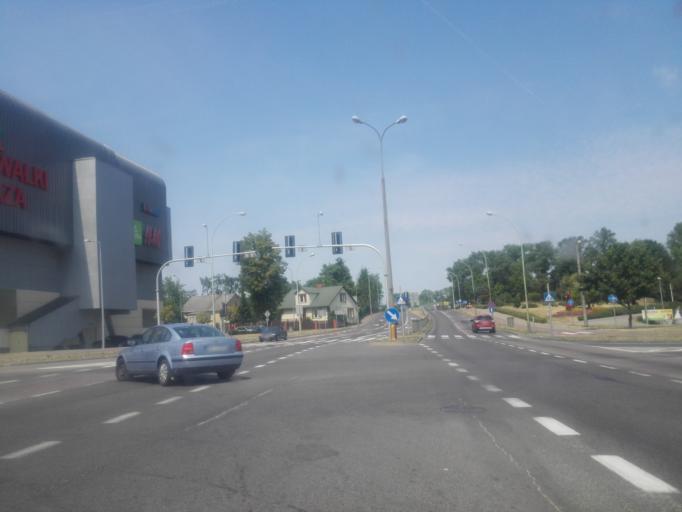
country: PL
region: Podlasie
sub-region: Suwalki
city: Suwalki
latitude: 54.1074
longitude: 22.9362
